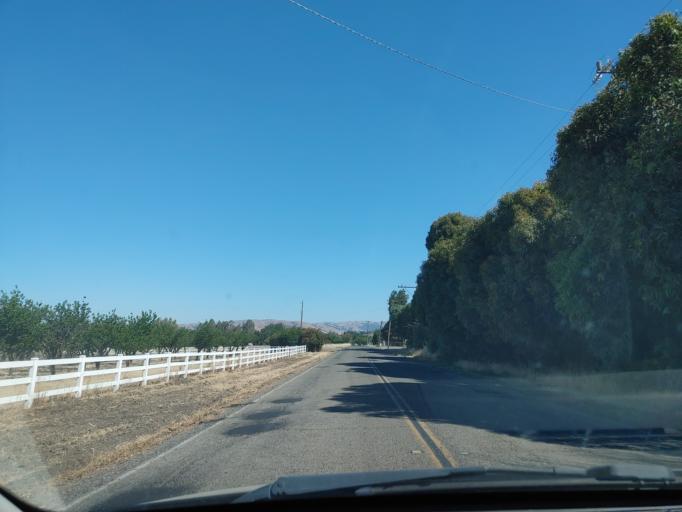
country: US
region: California
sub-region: San Benito County
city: Hollister
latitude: 36.9103
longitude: -121.3527
